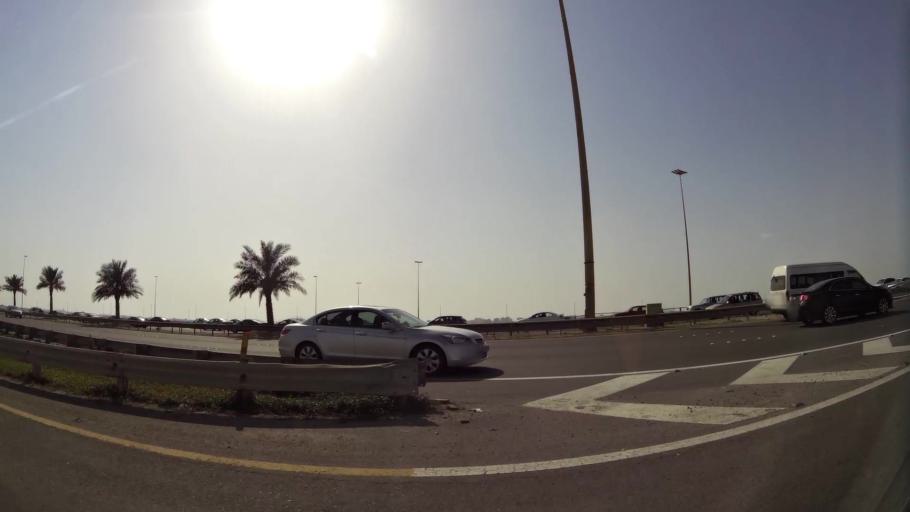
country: BH
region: Northern
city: Madinat `Isa
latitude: 26.1847
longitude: 50.5032
